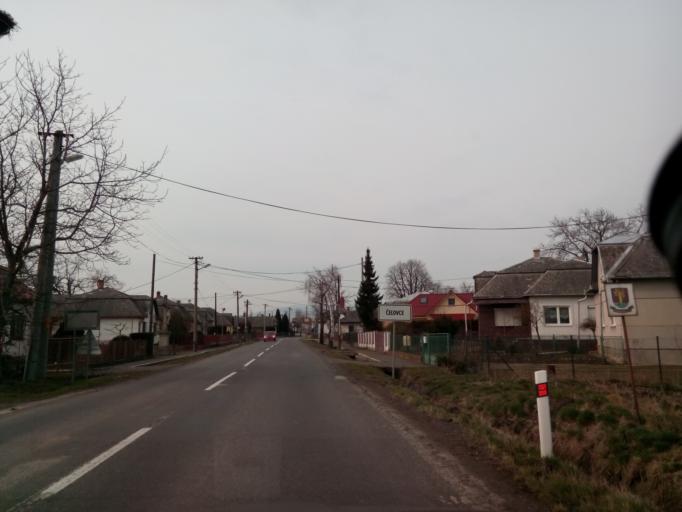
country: SK
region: Kosicky
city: Trebisov
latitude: 48.5973
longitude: 21.6313
